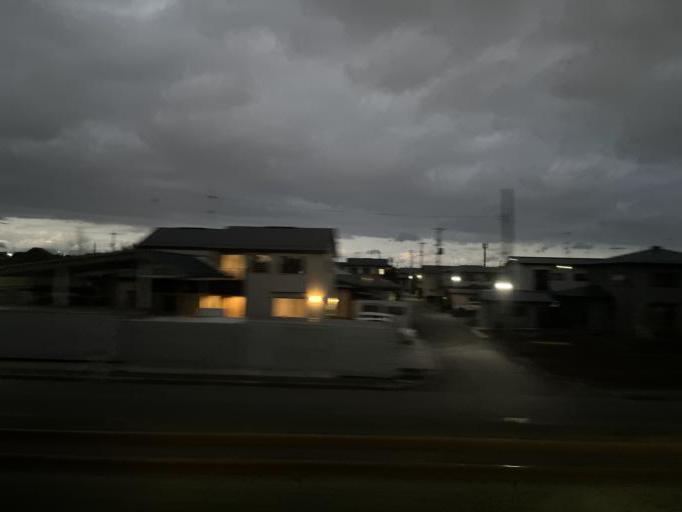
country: JP
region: Aomori
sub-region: Hachinohe Shi
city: Uchimaru
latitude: 40.5218
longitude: 141.4736
